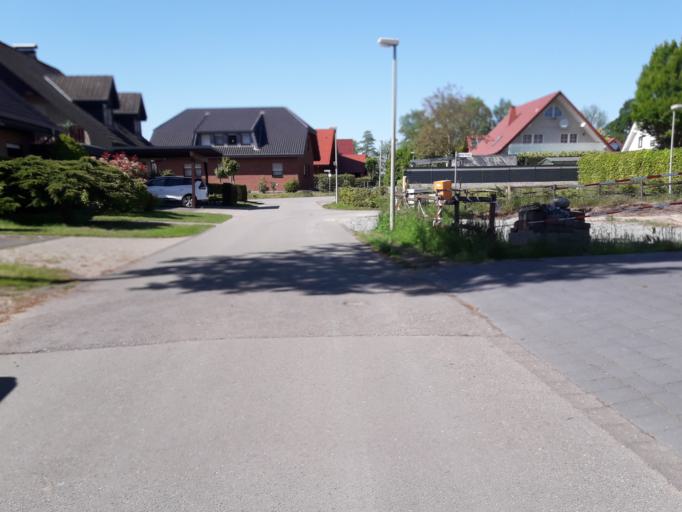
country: DE
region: North Rhine-Westphalia
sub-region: Regierungsbezirk Detmold
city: Delbruck
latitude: 51.7531
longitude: 8.5946
